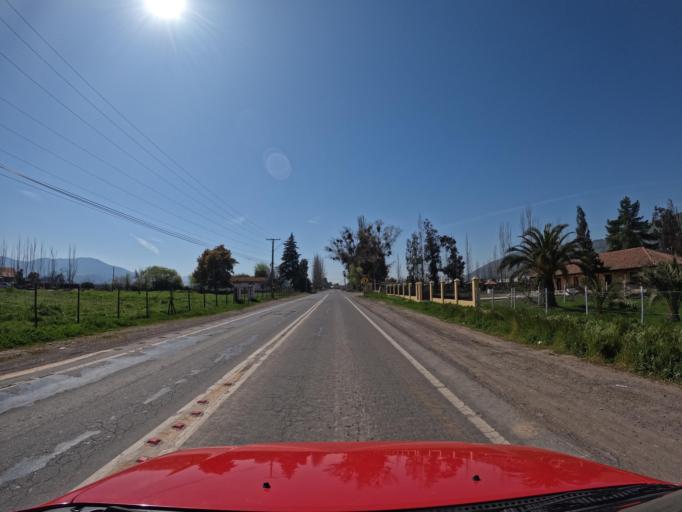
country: CL
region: Maule
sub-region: Provincia de Curico
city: Rauco
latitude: -35.0225
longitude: -71.4311
